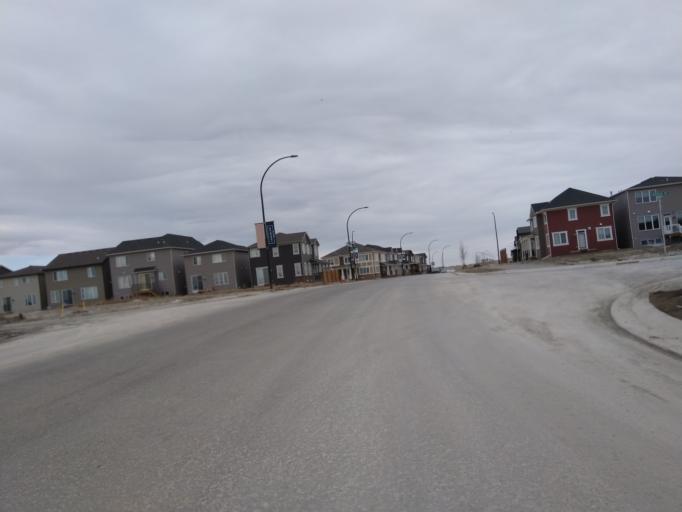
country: CA
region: Alberta
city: Calgary
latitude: 51.1793
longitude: -114.0900
